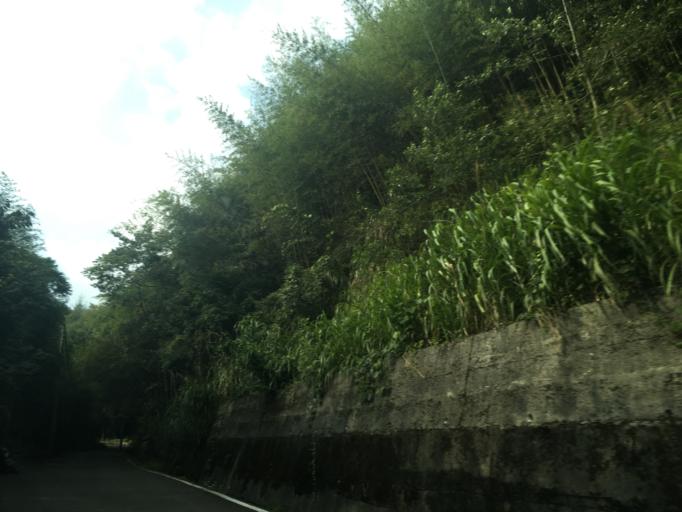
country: TW
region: Taiwan
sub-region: Miaoli
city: Miaoli
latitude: 24.3990
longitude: 120.9780
